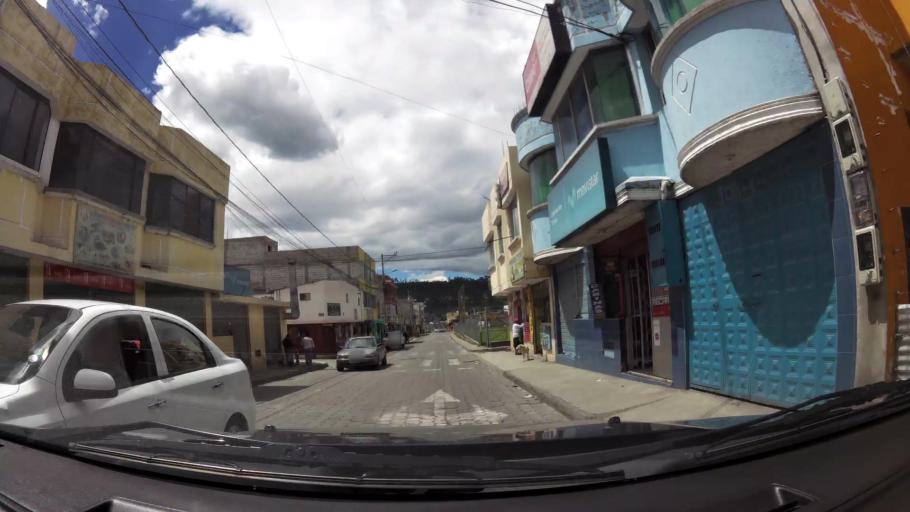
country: EC
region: Pichincha
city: Sangolqui
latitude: -0.3354
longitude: -78.5408
